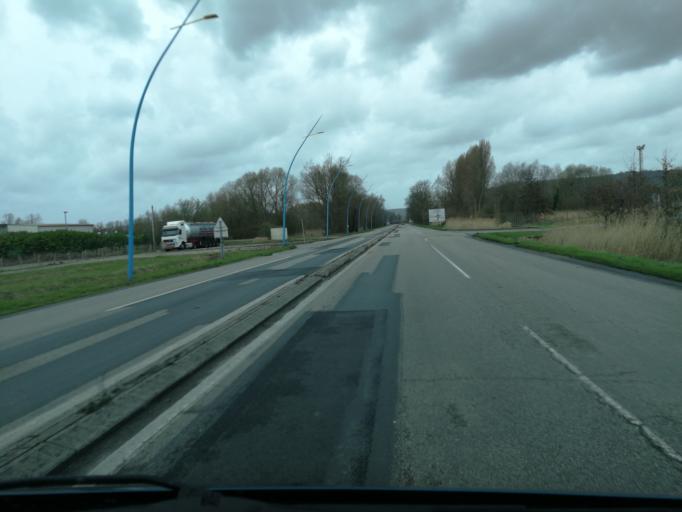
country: FR
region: Haute-Normandie
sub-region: Departement de l'Eure
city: Quillebeuf-sur-Seine
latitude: 49.4811
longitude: 0.5330
